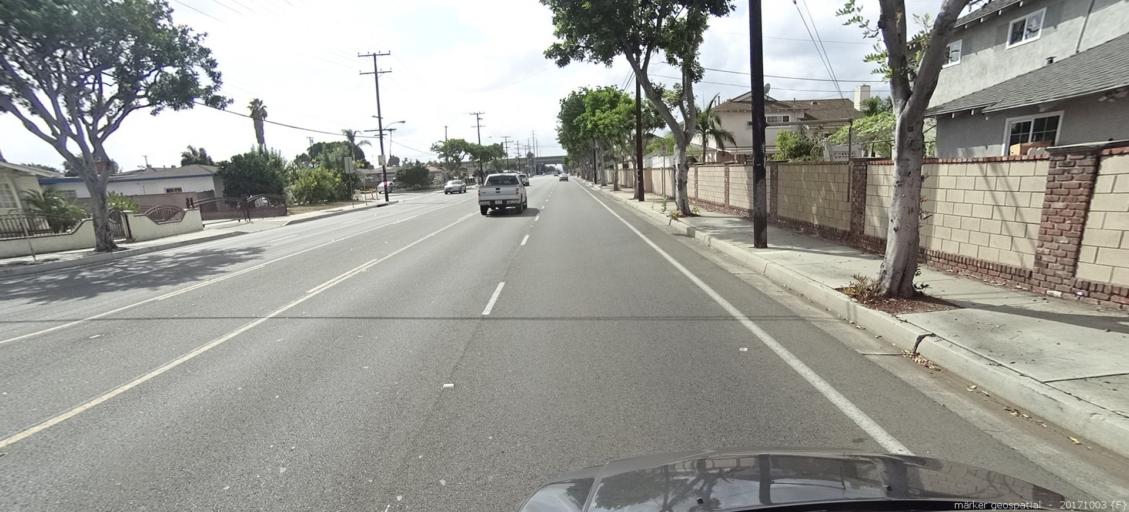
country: US
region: California
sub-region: Orange County
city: Garden Grove
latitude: 33.7699
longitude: -117.9291
